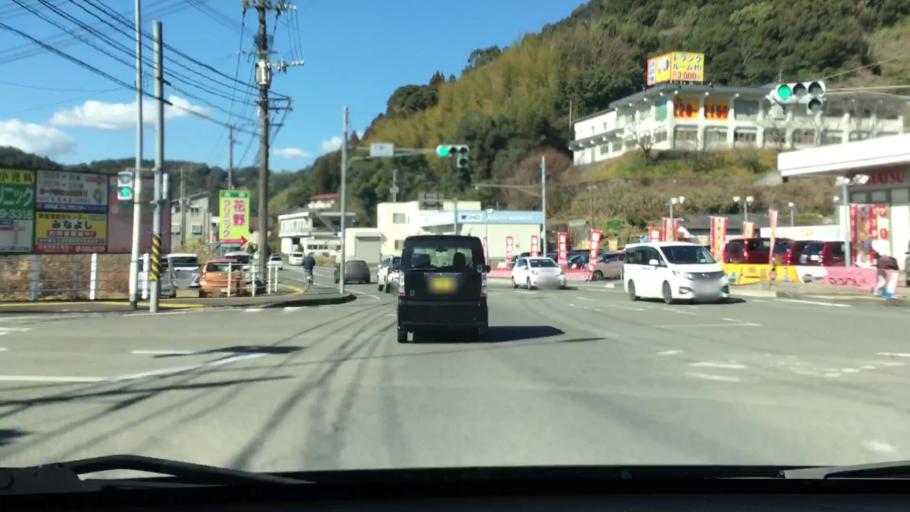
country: JP
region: Kagoshima
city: Kagoshima-shi
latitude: 31.6387
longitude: 130.5190
